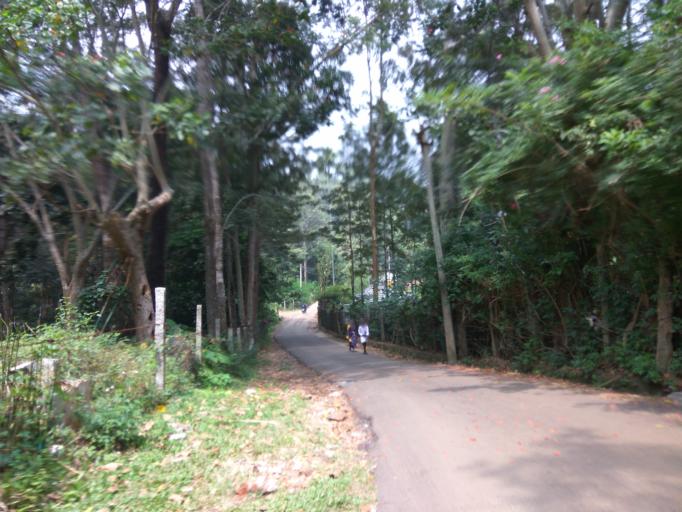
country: IN
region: Tamil Nadu
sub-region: Salem
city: Salem
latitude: 11.7919
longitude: 78.2024
